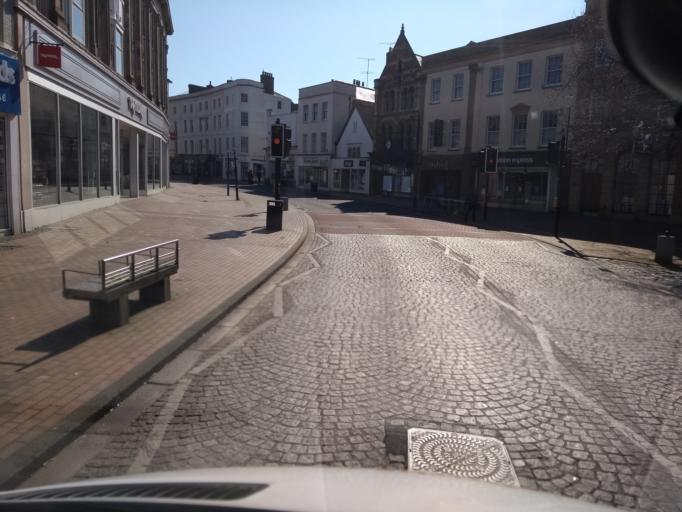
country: GB
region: England
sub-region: Somerset
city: Taunton
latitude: 51.0147
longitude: -3.1025
